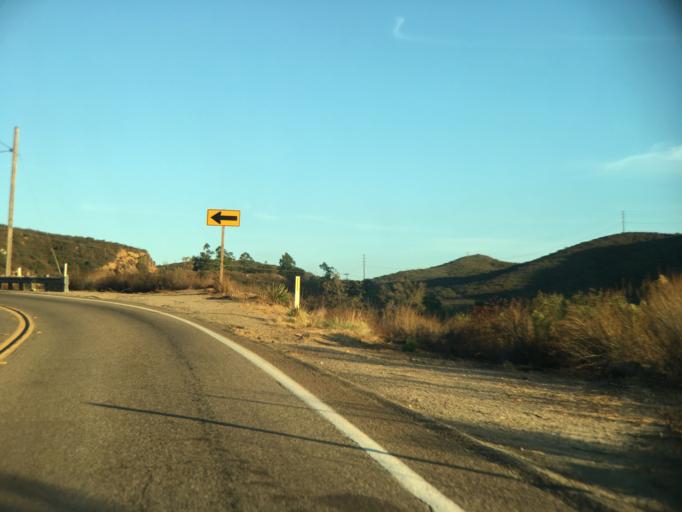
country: US
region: California
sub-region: San Diego County
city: Alpine
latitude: 32.8050
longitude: -116.7845
